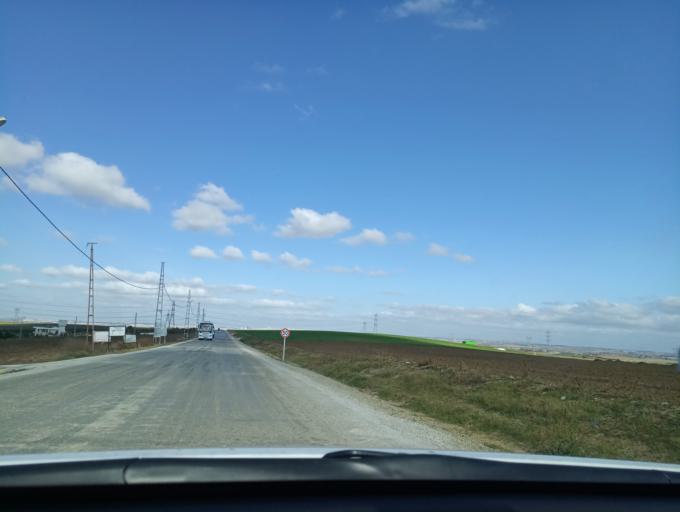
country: TR
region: Tekirdag
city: Corlu
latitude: 41.0519
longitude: 27.8353
